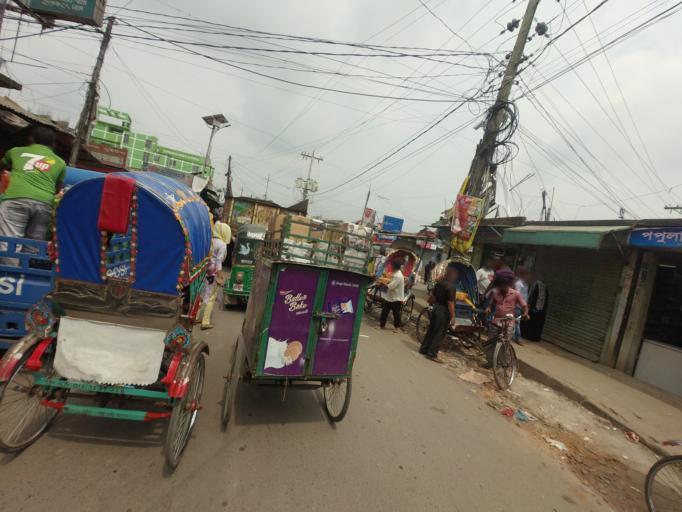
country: BD
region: Dhaka
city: Azimpur
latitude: 23.7303
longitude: 90.3342
